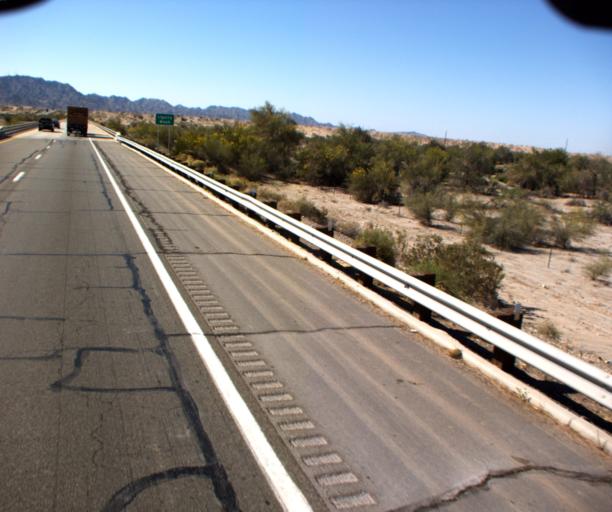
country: US
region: Arizona
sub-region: Yuma County
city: Wellton
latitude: 32.6593
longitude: -114.2514
